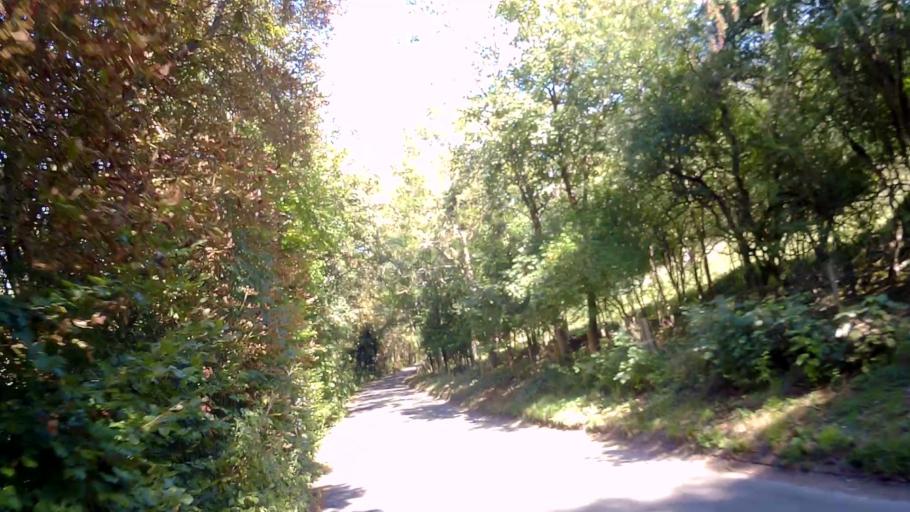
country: GB
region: England
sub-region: Hampshire
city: Andover
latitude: 51.1514
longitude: -1.4517
